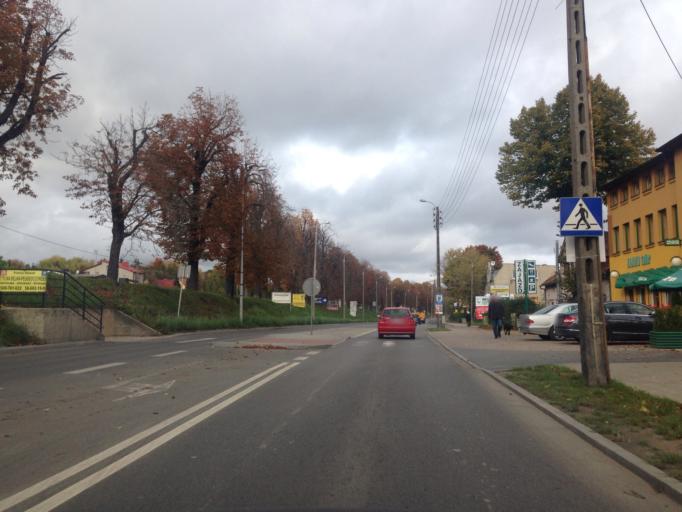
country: PL
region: Pomeranian Voivodeship
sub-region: Gdansk
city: Gdansk
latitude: 54.3148
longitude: 18.6292
